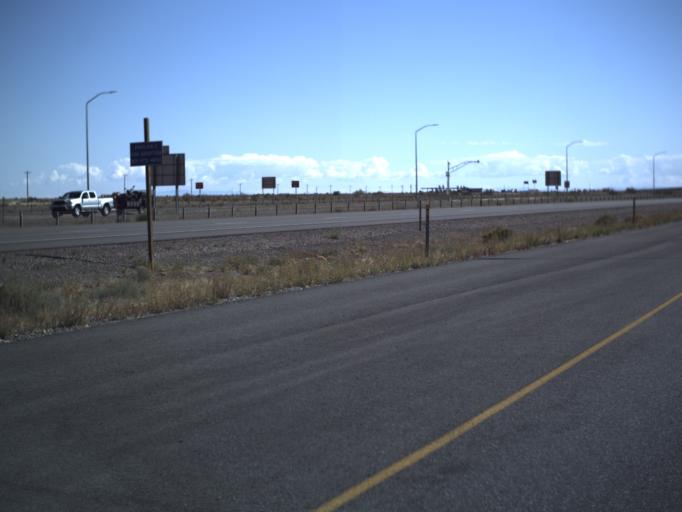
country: US
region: Utah
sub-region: Tooele County
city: Wendover
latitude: 40.7446
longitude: -113.9895
